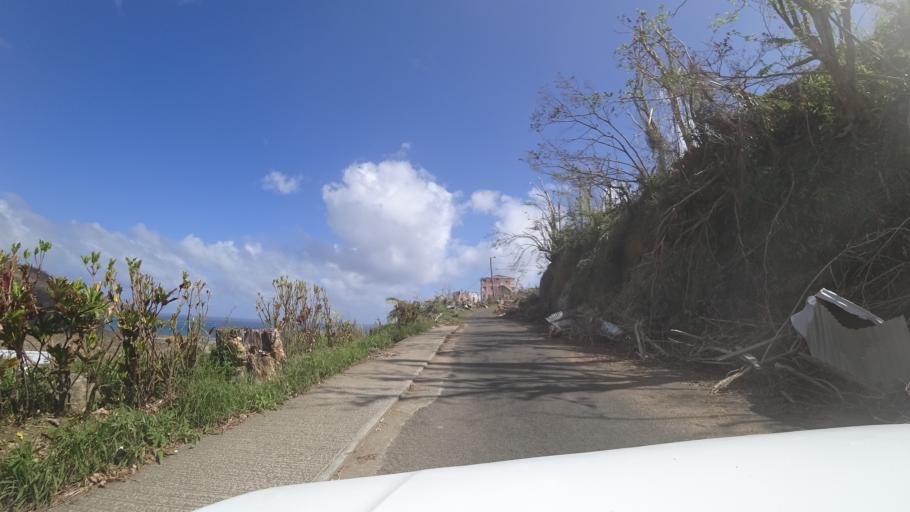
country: DM
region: Saint Patrick
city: Berekua
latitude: 15.2460
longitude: -61.3156
